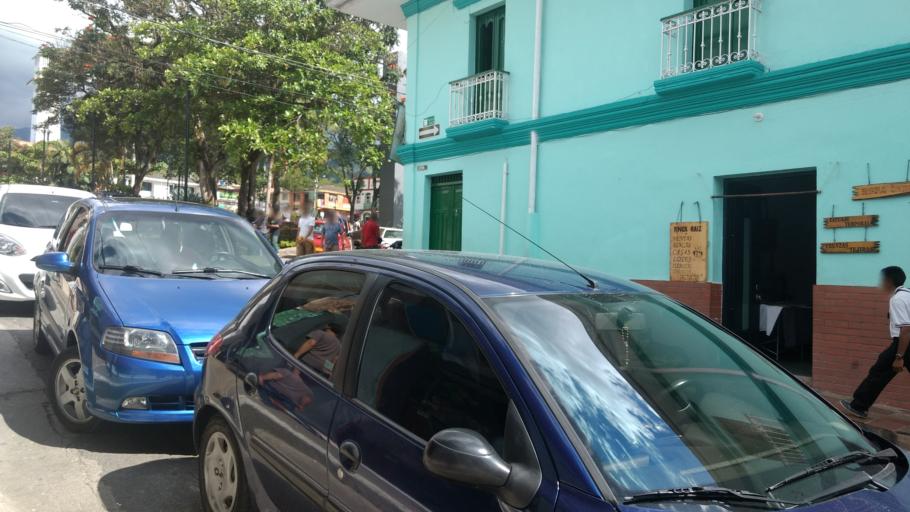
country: CO
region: Cundinamarca
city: La Vega
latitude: 5.0004
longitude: -74.3396
